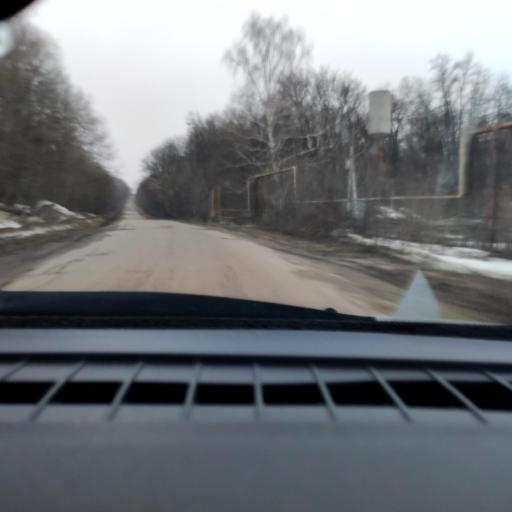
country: RU
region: Samara
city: Novosemeykino
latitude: 53.3344
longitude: 50.2692
